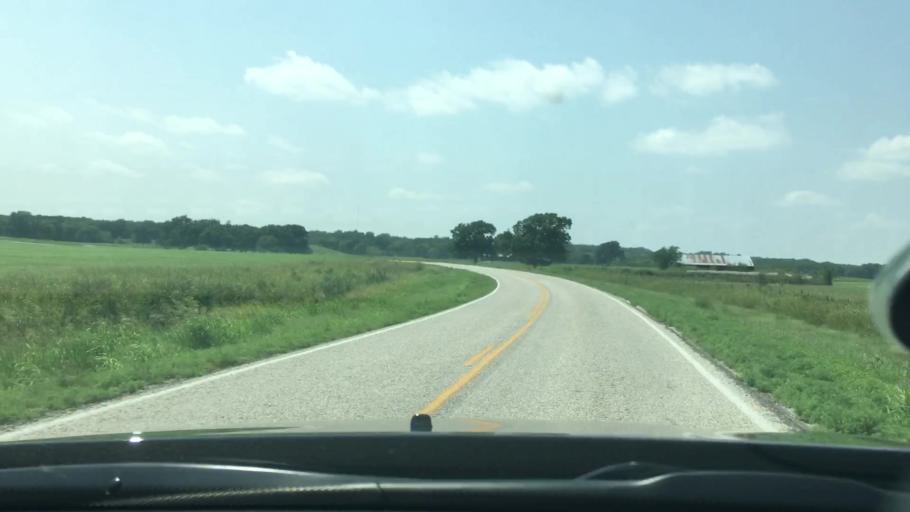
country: US
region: Oklahoma
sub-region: Johnston County
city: Tishomingo
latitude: 34.3762
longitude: -96.4899
